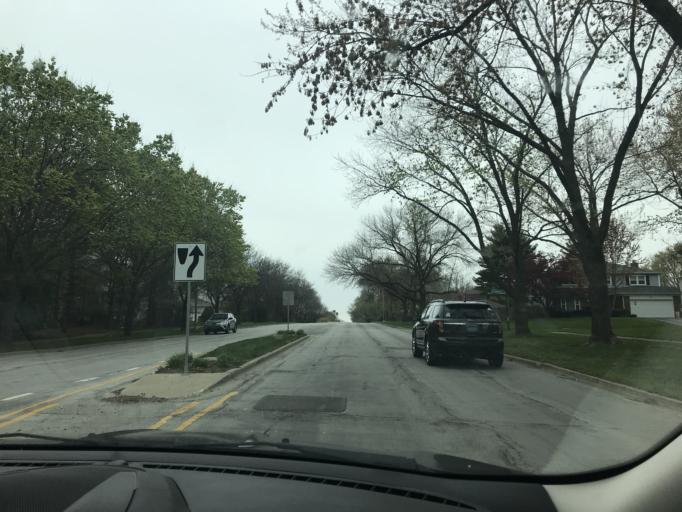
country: US
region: Illinois
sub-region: DuPage County
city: Naperville
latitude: 41.7411
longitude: -88.1180
